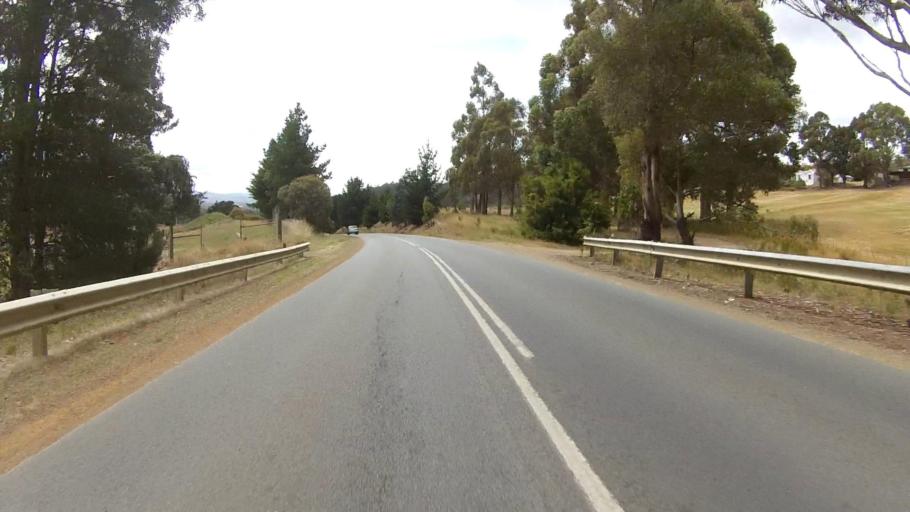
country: AU
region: Tasmania
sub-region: Kingborough
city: Kettering
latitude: -43.0904
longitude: 147.2496
